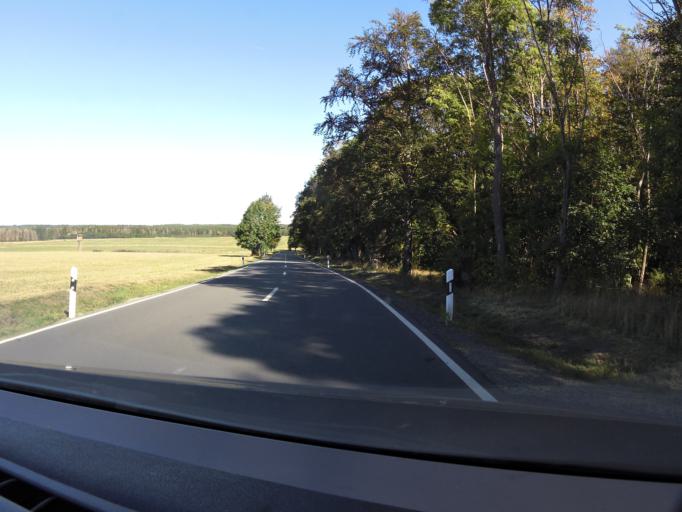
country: DE
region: Saxony-Anhalt
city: Hasselfelde
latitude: 51.6749
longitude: 10.8987
